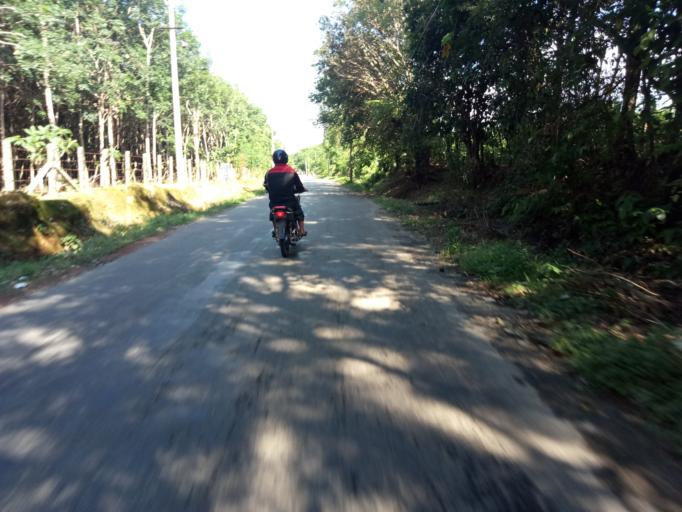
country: MM
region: Mon
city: Mawlamyine
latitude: 16.3793
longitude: 97.5513
